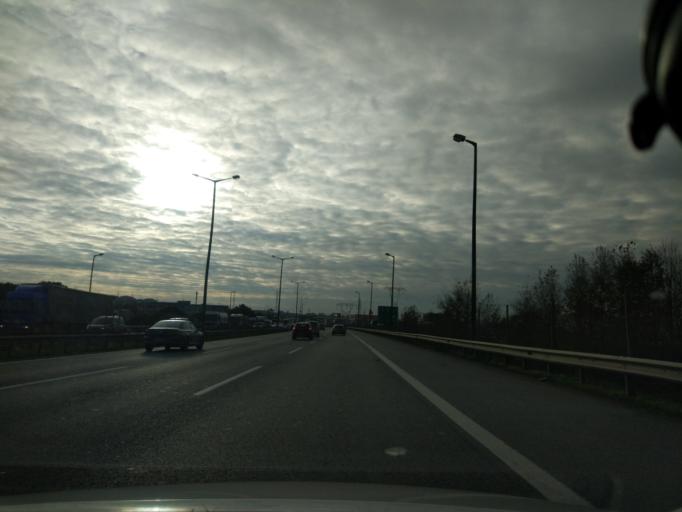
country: TR
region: Istanbul
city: Icmeler
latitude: 40.9130
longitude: 29.3558
